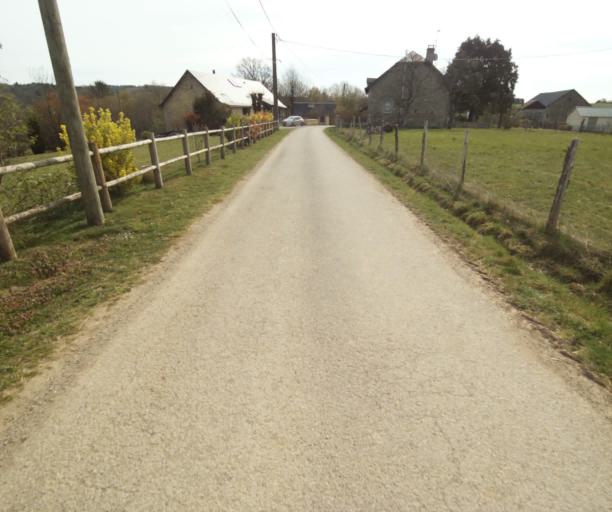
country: FR
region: Limousin
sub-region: Departement de la Correze
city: Correze
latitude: 45.3943
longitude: 1.8075
